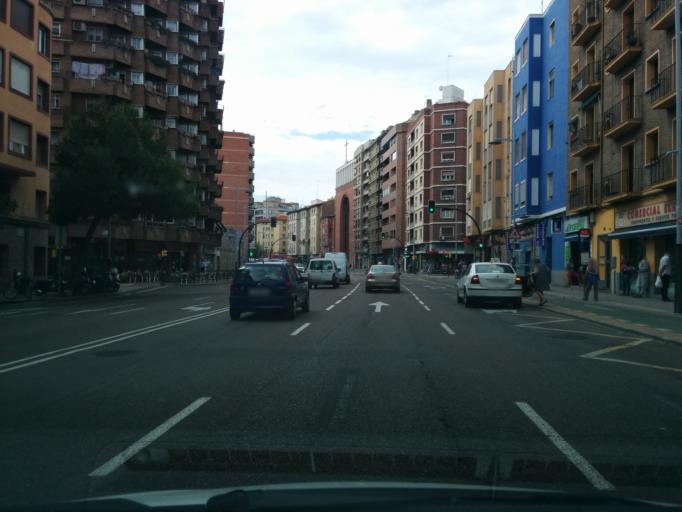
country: ES
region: Aragon
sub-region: Provincia de Zaragoza
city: Delicias
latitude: 41.6470
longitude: -0.8938
